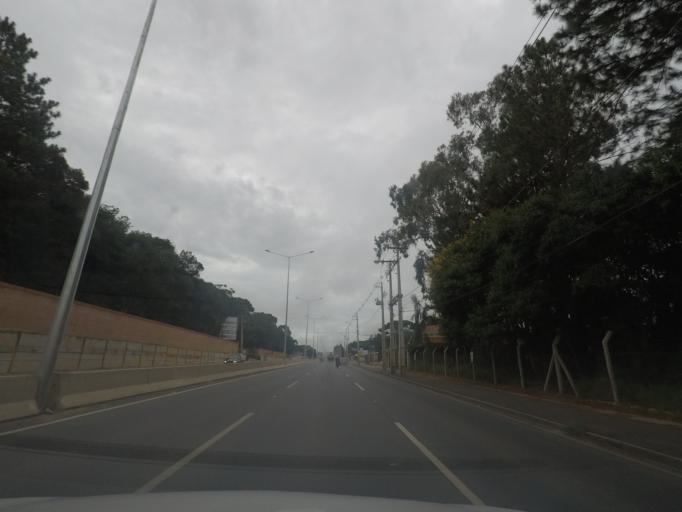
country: BR
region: Parana
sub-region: Piraquara
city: Piraquara
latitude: -25.4547
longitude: -49.1115
